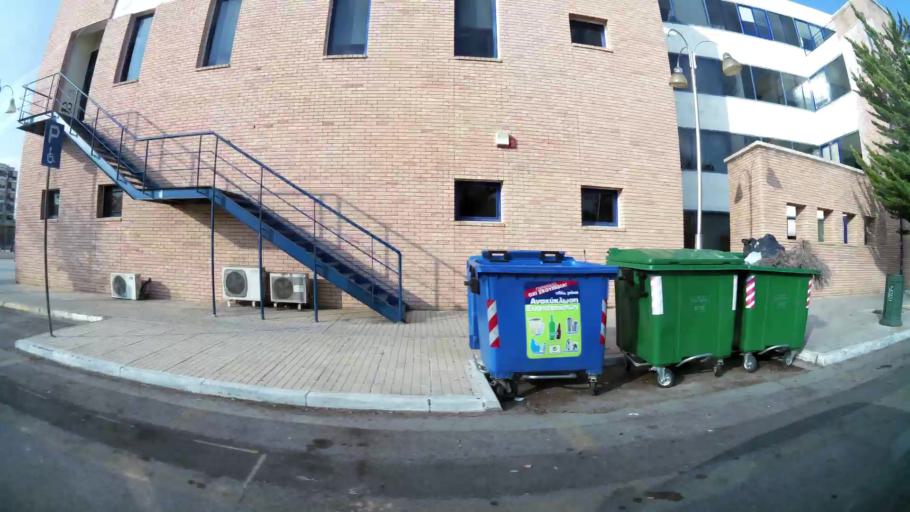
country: GR
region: Attica
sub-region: Nomarchia Anatolikis Attikis
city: Acharnes
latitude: 38.0745
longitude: 23.7408
